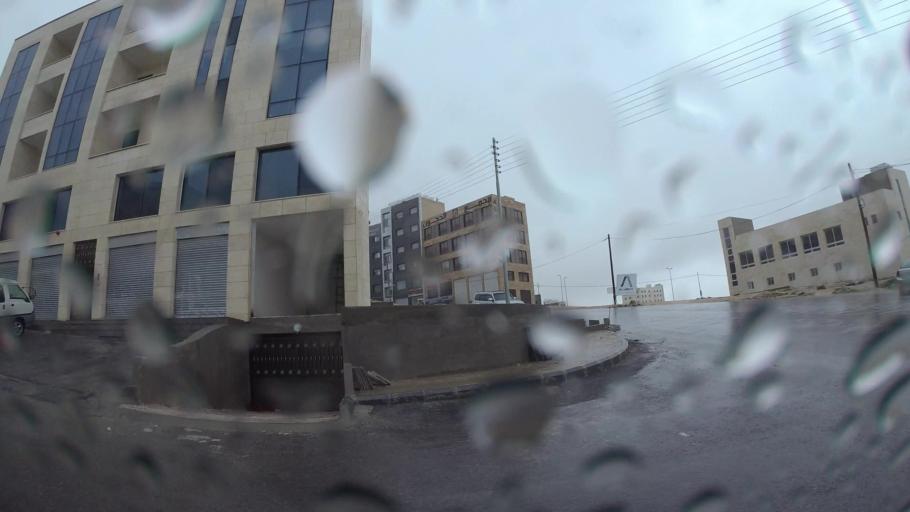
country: JO
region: Amman
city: Al Jubayhah
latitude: 32.0491
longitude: 35.8828
